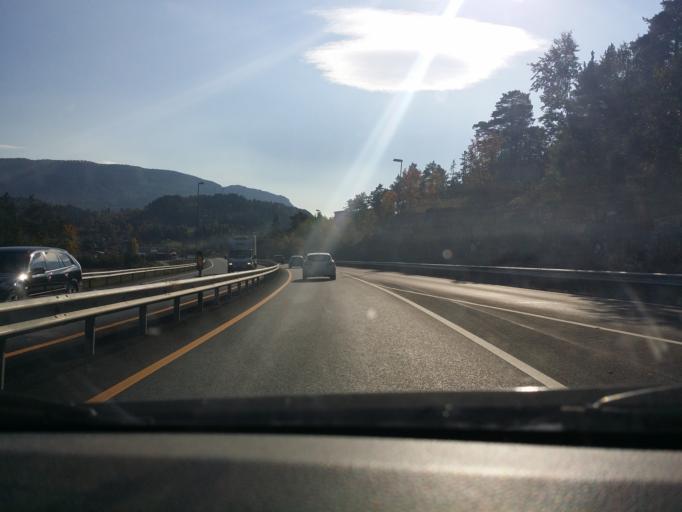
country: NO
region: Buskerud
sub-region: Hole
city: Vik
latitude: 60.0865
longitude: 10.2864
